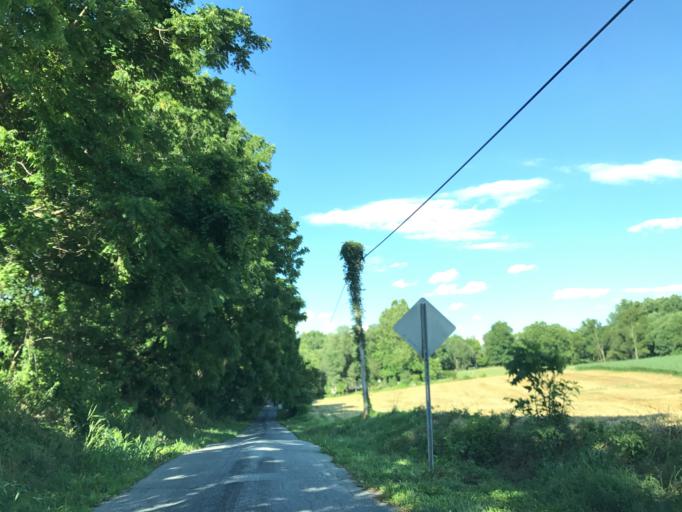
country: US
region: Pennsylvania
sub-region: Lancaster County
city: Conestoga
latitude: 39.9226
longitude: -76.3311
